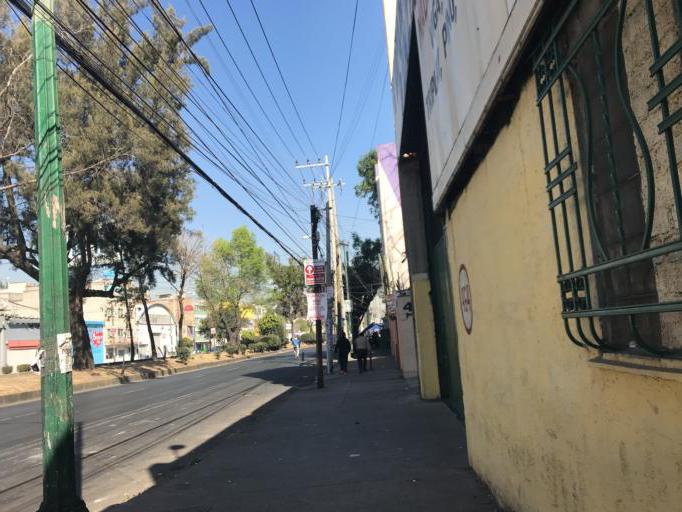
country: MX
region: Mexico City
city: Colonia Nativitas
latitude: 19.4022
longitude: -99.1251
